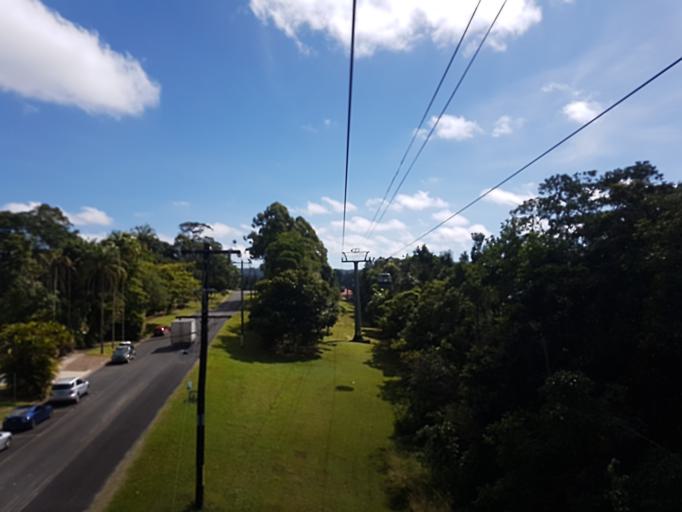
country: AU
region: Queensland
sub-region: Tablelands
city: Kuranda
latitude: -16.8221
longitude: 145.6404
